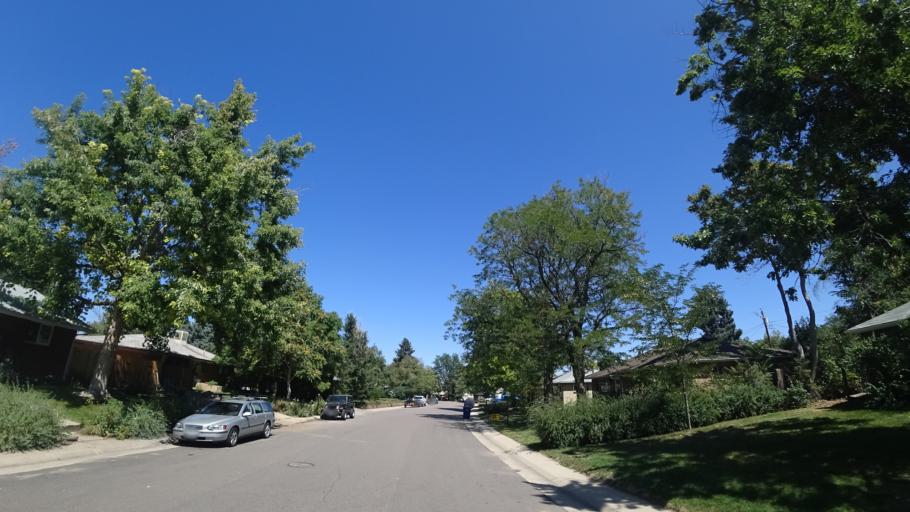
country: US
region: Colorado
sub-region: Arapahoe County
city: Littleton
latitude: 39.6111
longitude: -104.9934
